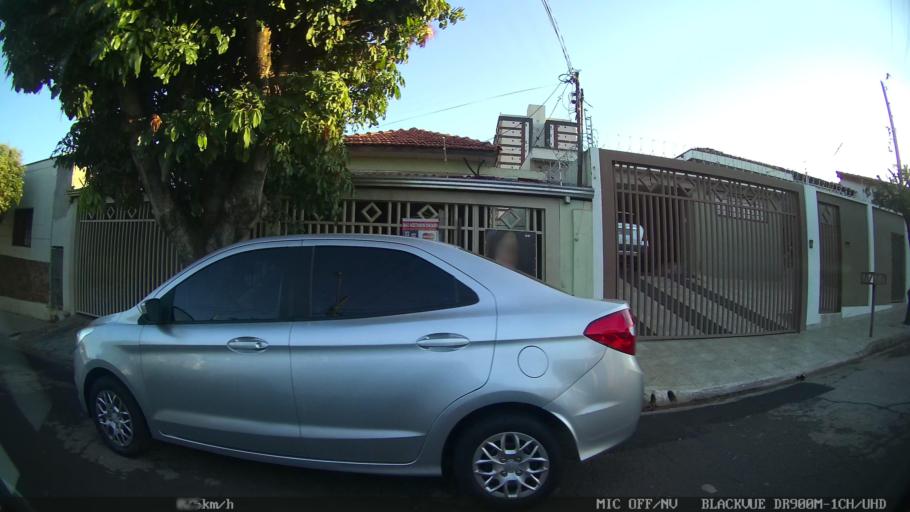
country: BR
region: Sao Paulo
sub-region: Sao Jose Do Rio Preto
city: Sao Jose do Rio Preto
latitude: -20.8012
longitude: -49.3806
